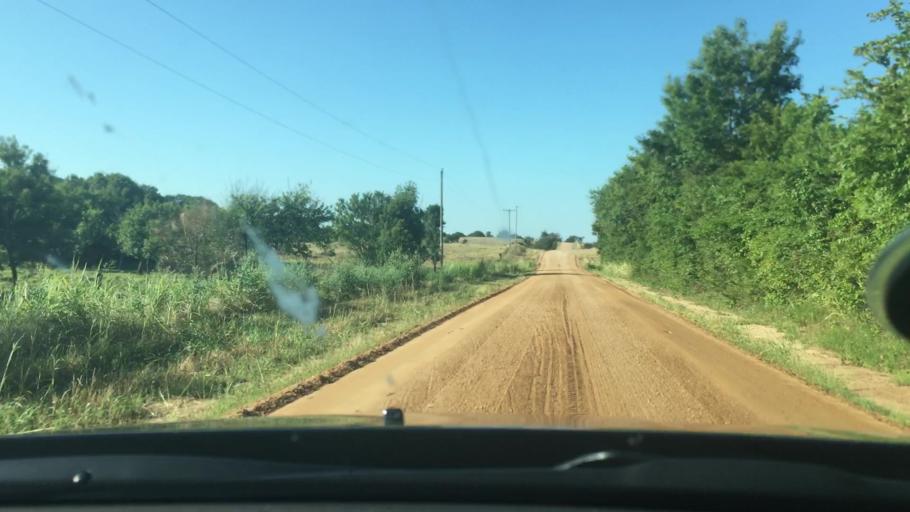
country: US
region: Oklahoma
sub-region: Murray County
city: Sulphur
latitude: 34.4067
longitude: -96.7936
